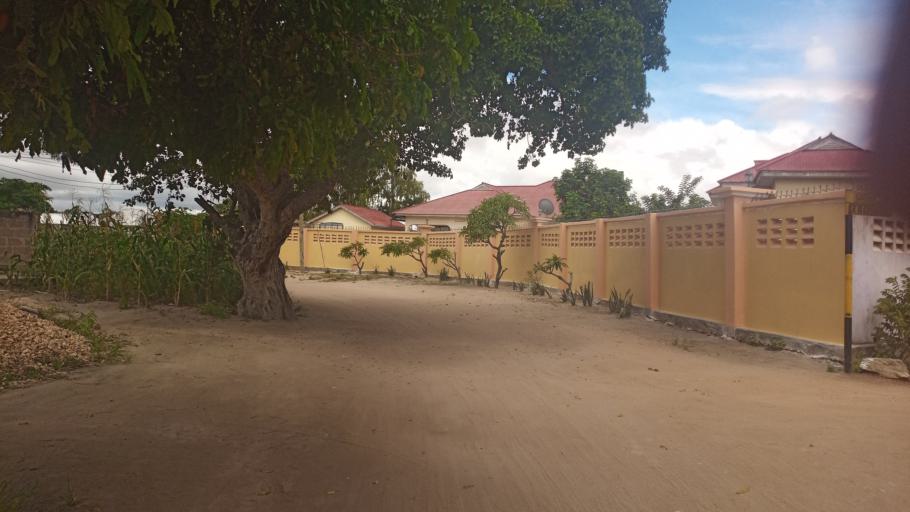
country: TZ
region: Dodoma
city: Dodoma
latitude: -6.1881
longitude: 35.7254
